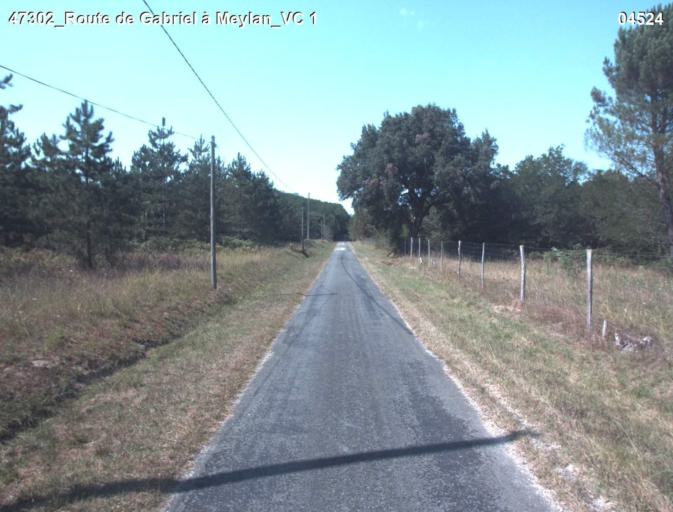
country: FR
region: Aquitaine
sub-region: Departement des Landes
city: Gabarret
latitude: 44.0807
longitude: 0.1130
